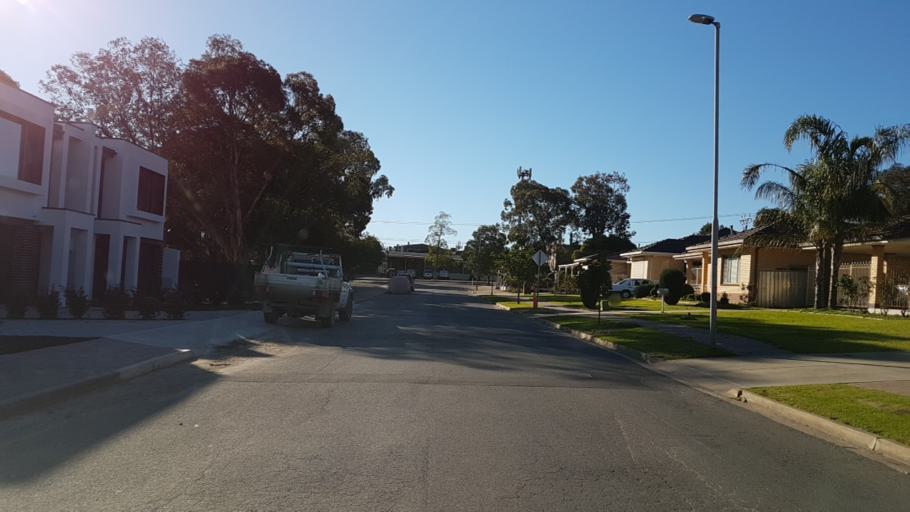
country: AU
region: South Australia
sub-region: Campbelltown
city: Paradise
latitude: -34.8820
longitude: 138.6842
